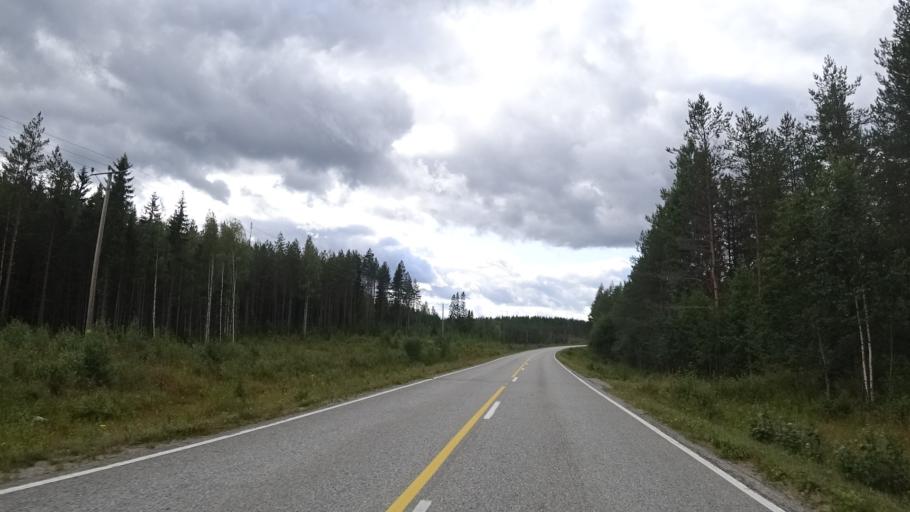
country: FI
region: North Karelia
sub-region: Joensuu
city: Ilomantsi
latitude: 62.6233
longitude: 31.2393
